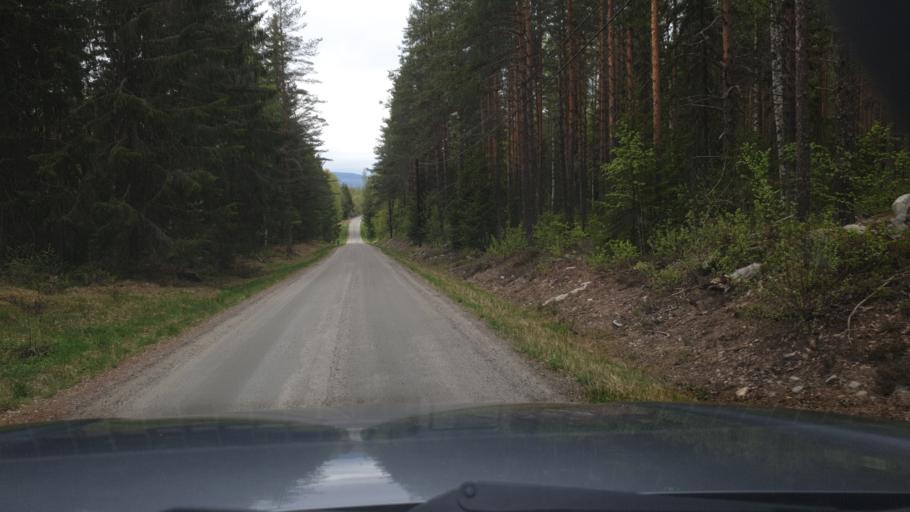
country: SE
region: Gaevleborg
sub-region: Ljusdals Kommun
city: Jaervsoe
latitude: 61.6567
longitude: 16.2707
